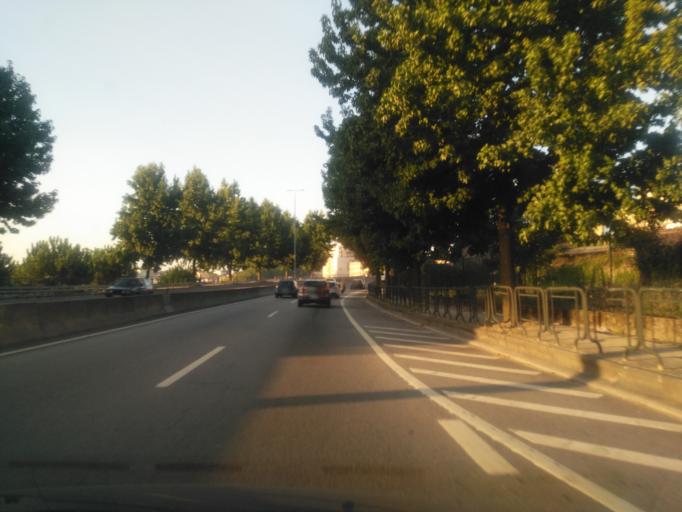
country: PT
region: Braga
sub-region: Braga
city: Braga
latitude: 41.5558
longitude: -8.4287
